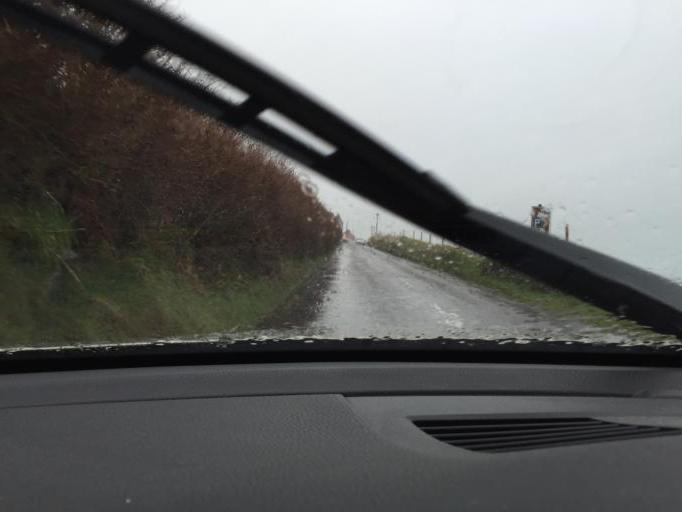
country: IE
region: Munster
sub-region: Ciarrai
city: Dingle
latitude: 52.1338
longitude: -10.3627
